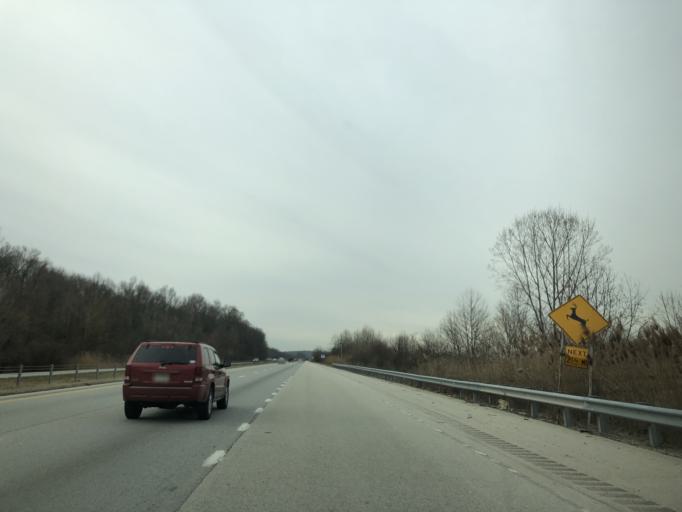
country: US
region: Pennsylvania
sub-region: Chester County
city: Exton
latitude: 40.0186
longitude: -75.6309
